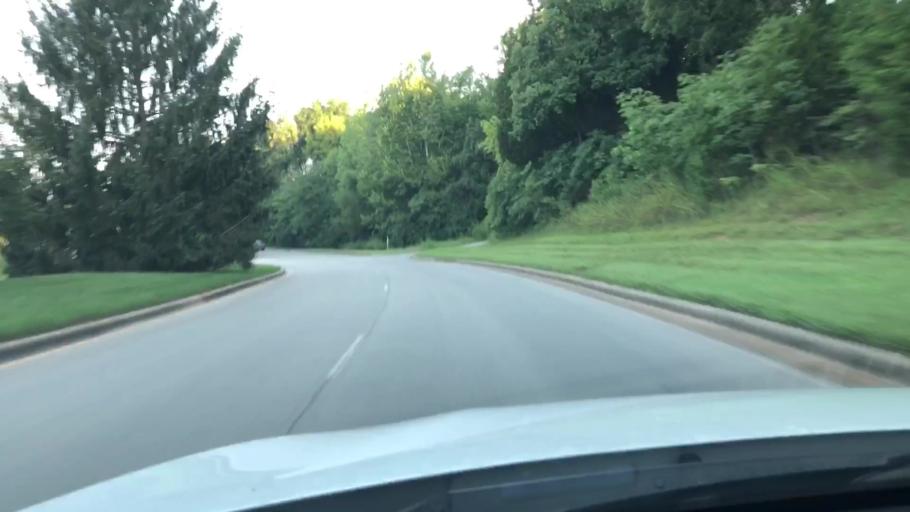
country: US
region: Kentucky
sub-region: Jefferson County
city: Douglass Hills
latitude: 38.2170
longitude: -85.5333
